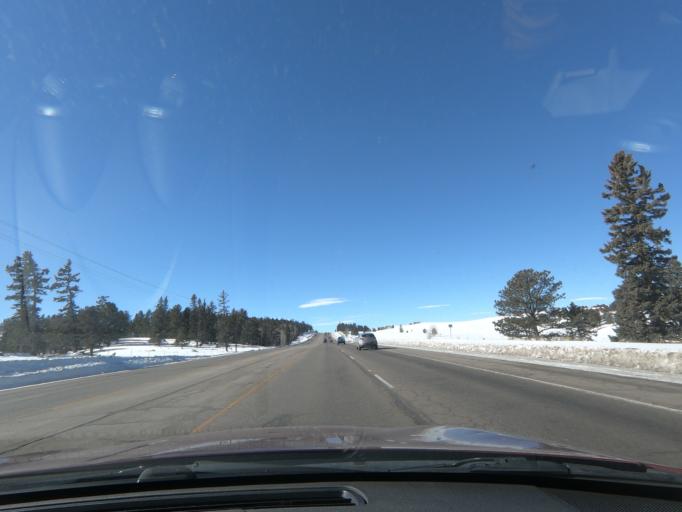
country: US
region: Colorado
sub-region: Teller County
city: Woodland Park
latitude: 38.9564
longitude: -105.1156
